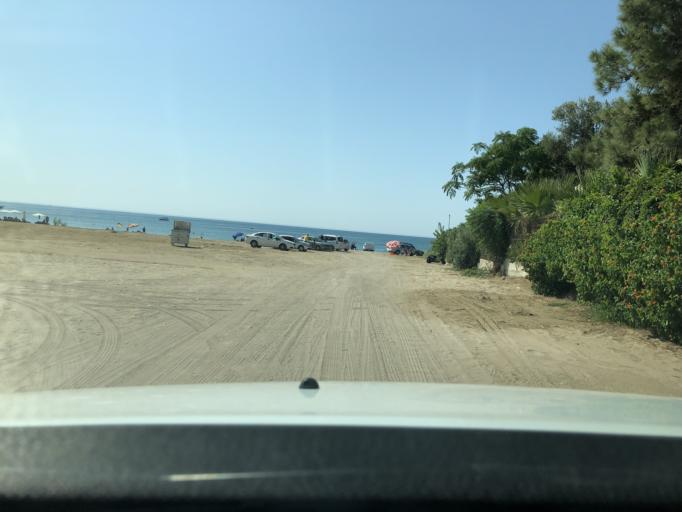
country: TR
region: Antalya
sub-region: Manavgat
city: Side
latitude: 36.7569
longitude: 31.4230
